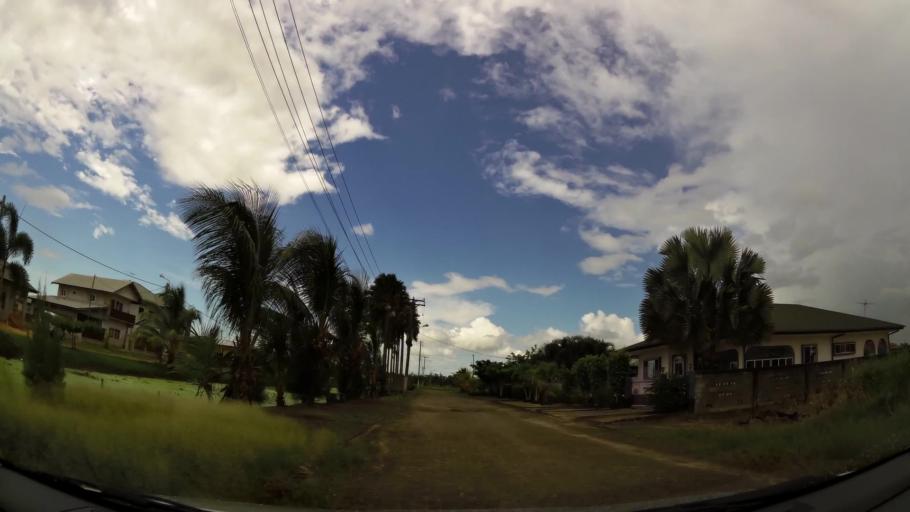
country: SR
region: Paramaribo
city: Paramaribo
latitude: 5.8627
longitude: -55.1239
